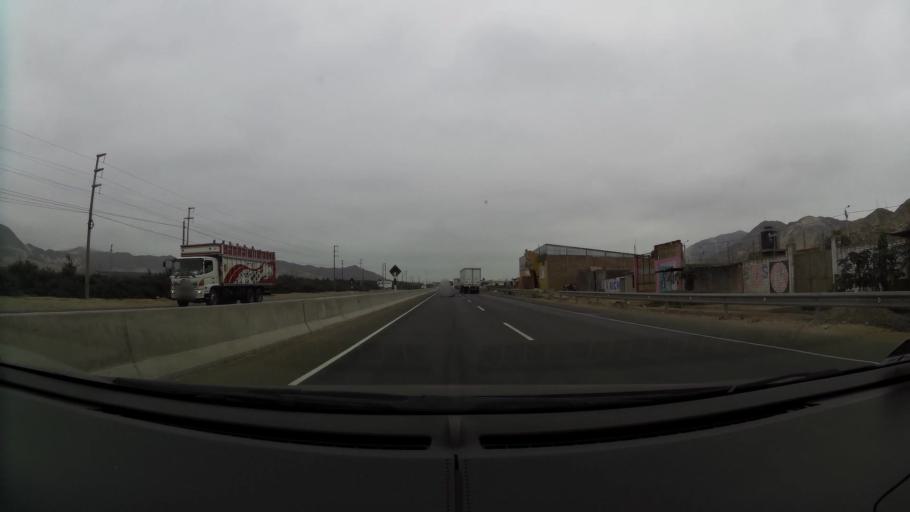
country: PE
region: La Libertad
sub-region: Viru
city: Chao
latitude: -8.5141
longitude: -78.6859
